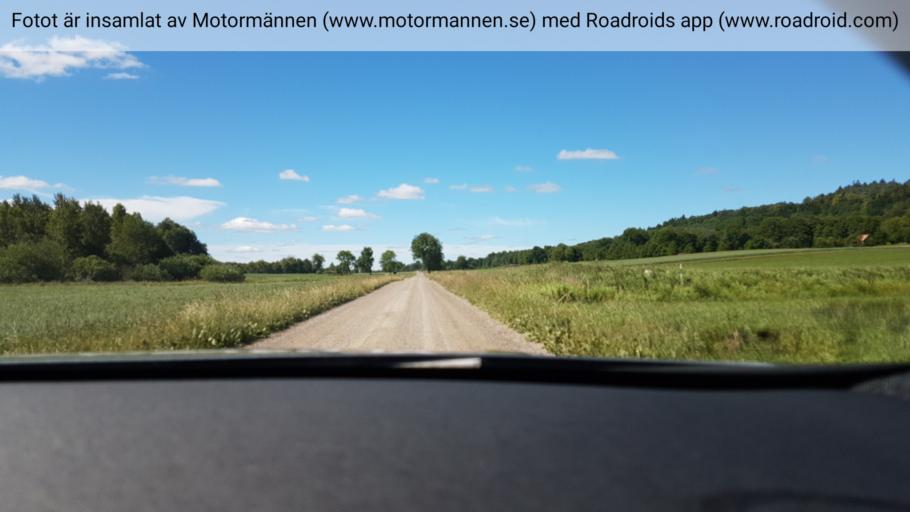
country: SE
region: Vaestra Goetaland
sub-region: Falkopings Kommun
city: Akarp
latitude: 58.2222
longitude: 13.7728
